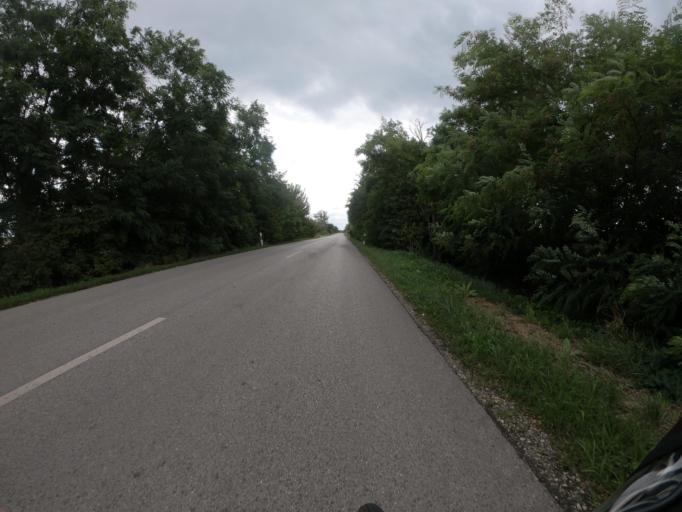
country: HU
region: Heves
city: Poroszlo
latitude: 47.6961
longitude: 20.7265
